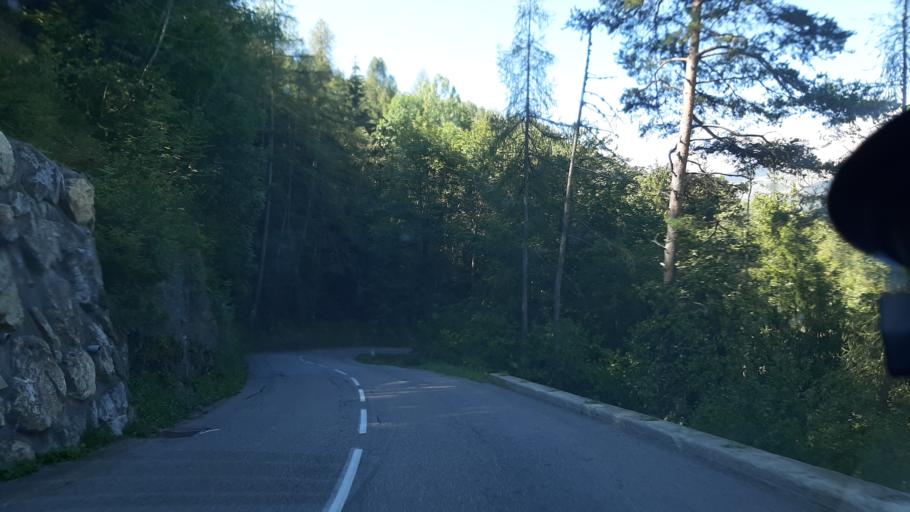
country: FR
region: Rhone-Alpes
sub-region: Departement de la Savoie
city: Aime
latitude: 45.5411
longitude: 6.6385
